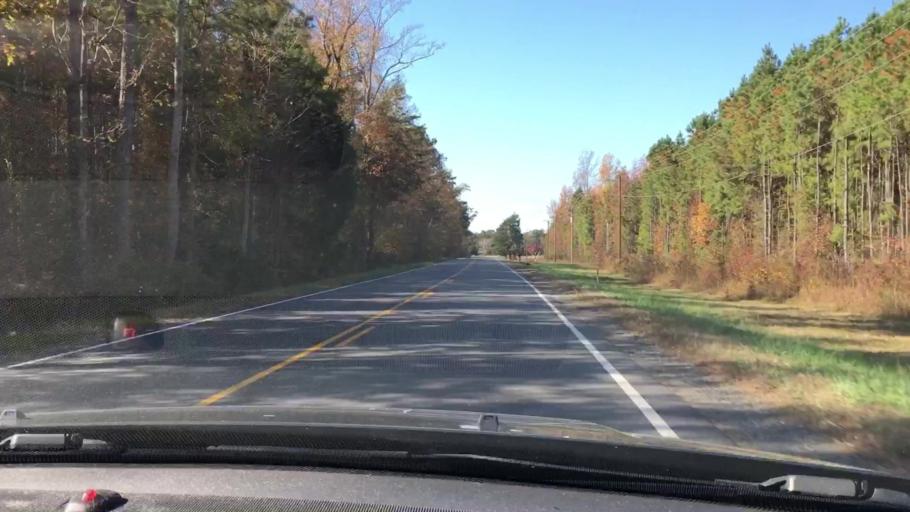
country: US
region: Virginia
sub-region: King William County
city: King William
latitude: 37.6582
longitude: -76.9530
